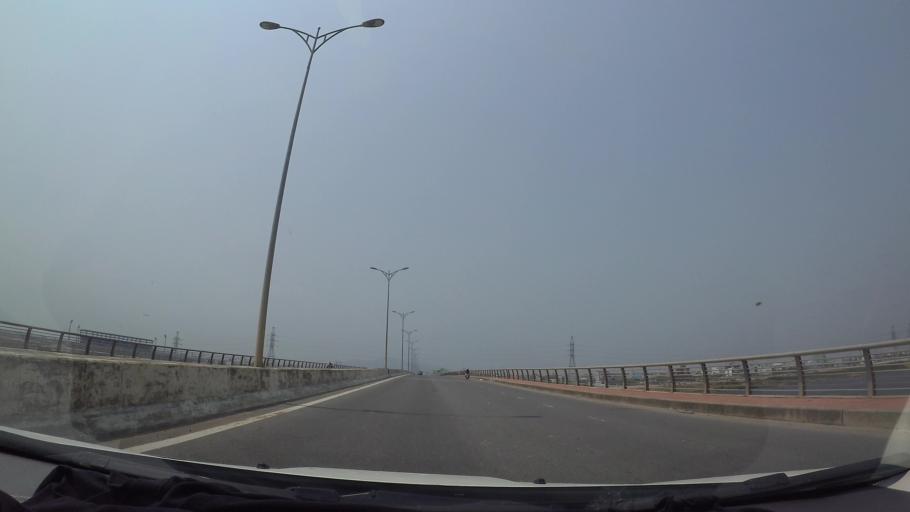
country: VN
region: Da Nang
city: Ngu Hanh Son
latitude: 16.0009
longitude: 108.2305
